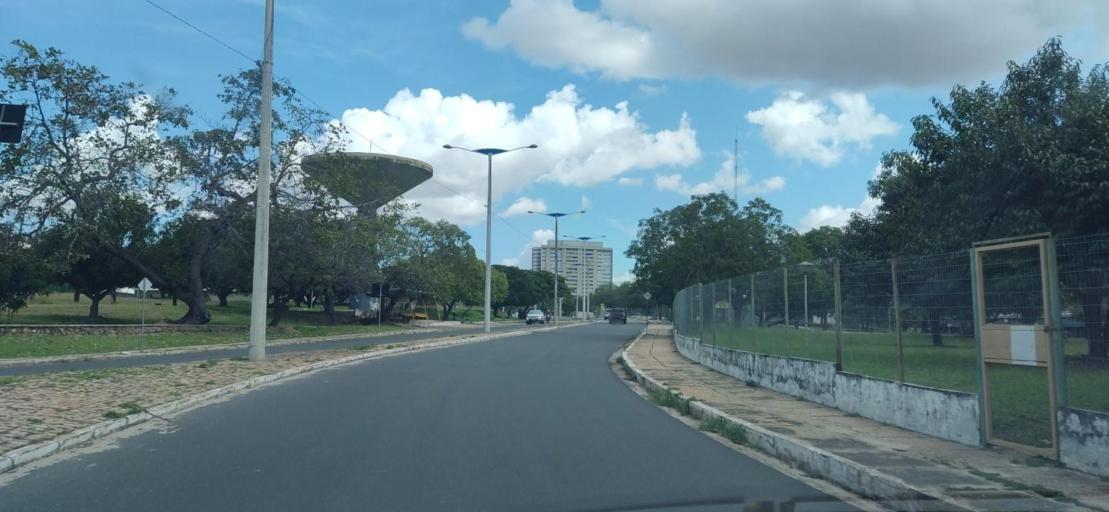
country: BR
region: Piaui
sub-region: Teresina
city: Teresina
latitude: -5.0580
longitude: -42.7949
